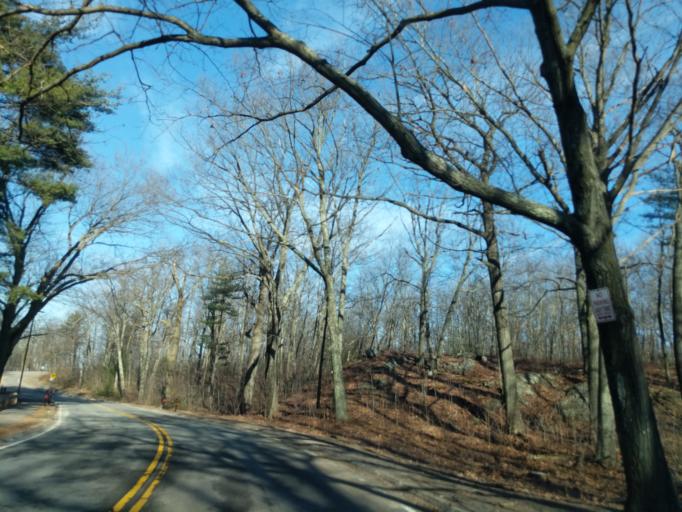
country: US
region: Massachusetts
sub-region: Worcester County
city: Hamilton
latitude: 42.2824
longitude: -71.7774
